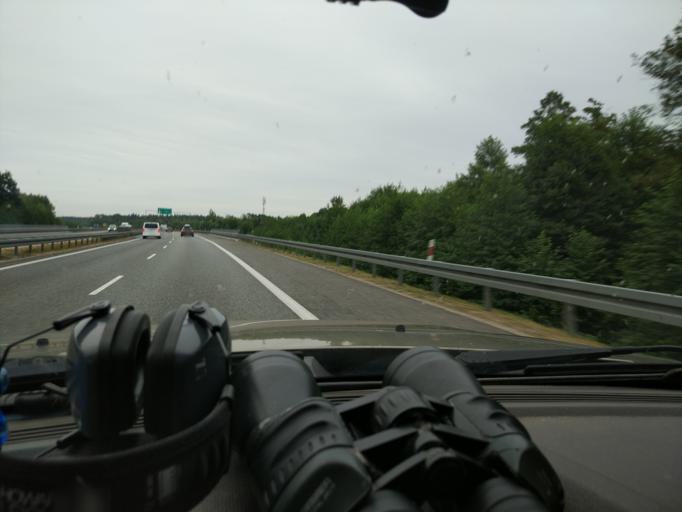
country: PL
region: Masovian Voivodeship
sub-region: Powiat wyszkowski
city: Wyszkow
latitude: 52.5796
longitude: 21.4936
